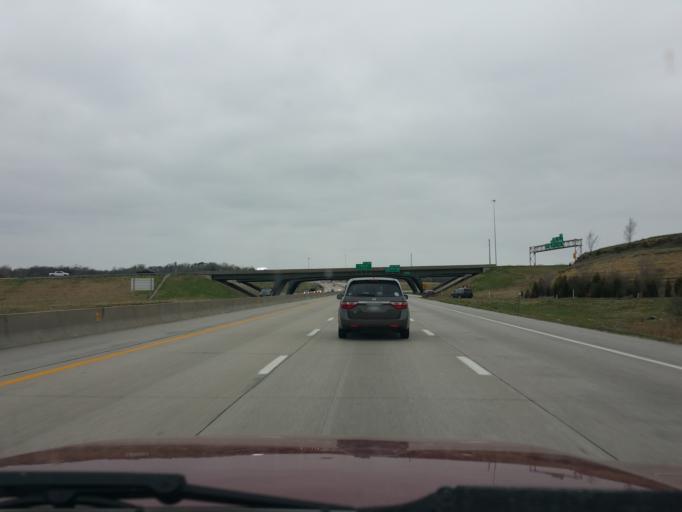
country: US
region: Kansas
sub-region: Wyandotte County
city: Edwardsville
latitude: 39.1065
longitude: -94.8084
